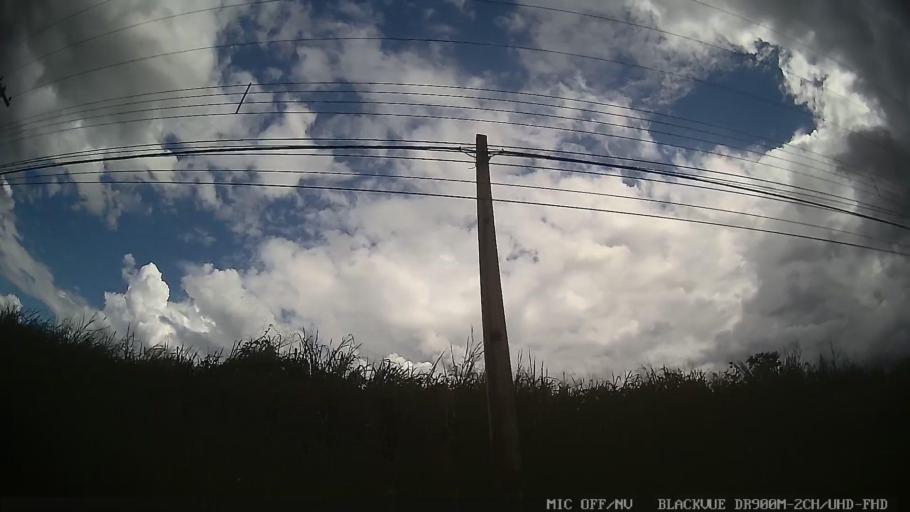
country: BR
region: Sao Paulo
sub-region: Jaguariuna
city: Jaguariuna
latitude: -22.6629
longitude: -46.9496
